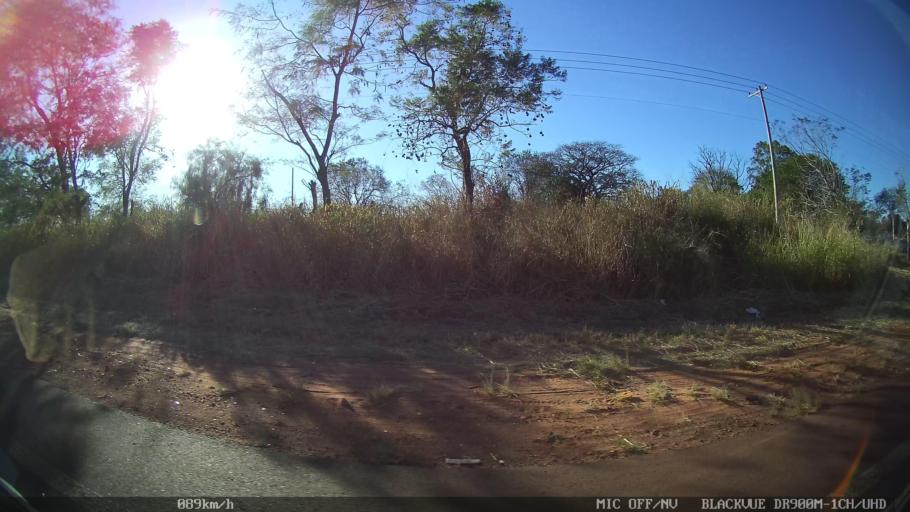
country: BR
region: Sao Paulo
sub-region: Olimpia
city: Olimpia
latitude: -20.7097
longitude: -48.9721
